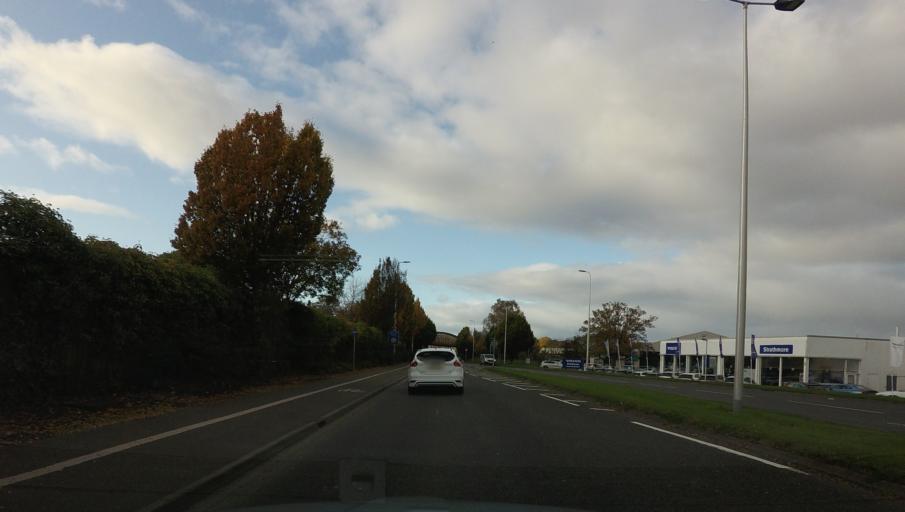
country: GB
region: Scotland
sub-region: Perth and Kinross
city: Perth
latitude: 56.4144
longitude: -3.4584
